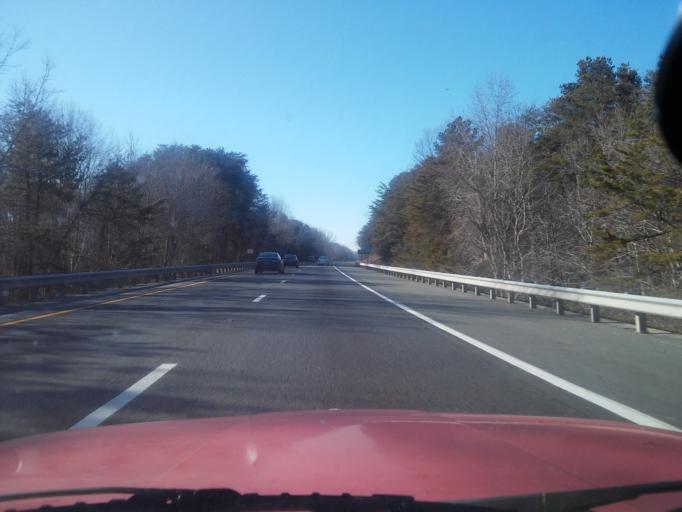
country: US
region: Virginia
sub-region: Fluvanna County
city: Lake Monticello
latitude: 37.9993
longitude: -78.3452
